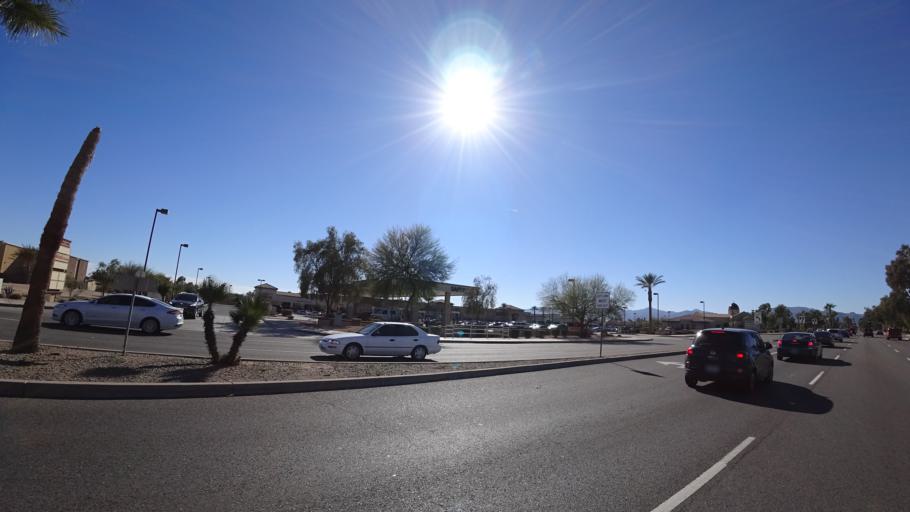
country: US
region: Arizona
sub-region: Maricopa County
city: Sun City West
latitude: 33.6389
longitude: -112.4240
